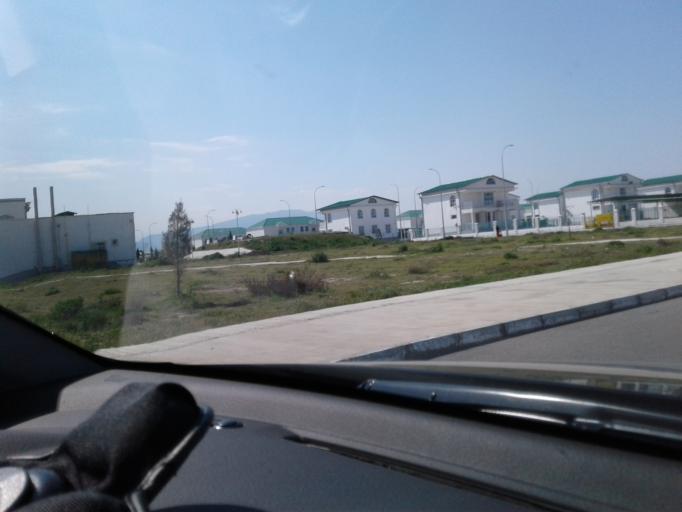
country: TM
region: Ahal
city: Abadan
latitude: 38.0786
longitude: 58.2822
